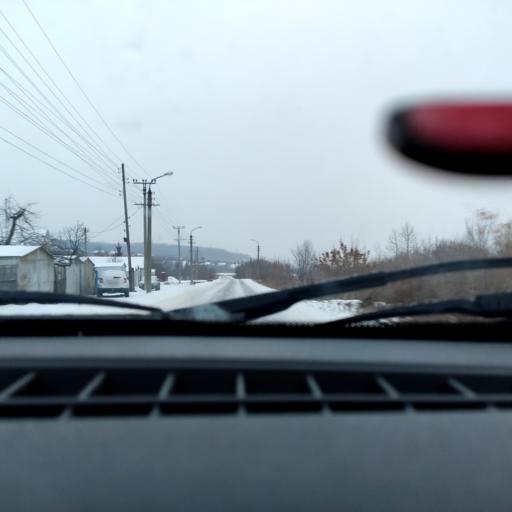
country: RU
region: Bashkortostan
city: Blagoveshchensk
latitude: 54.8917
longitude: 56.0324
